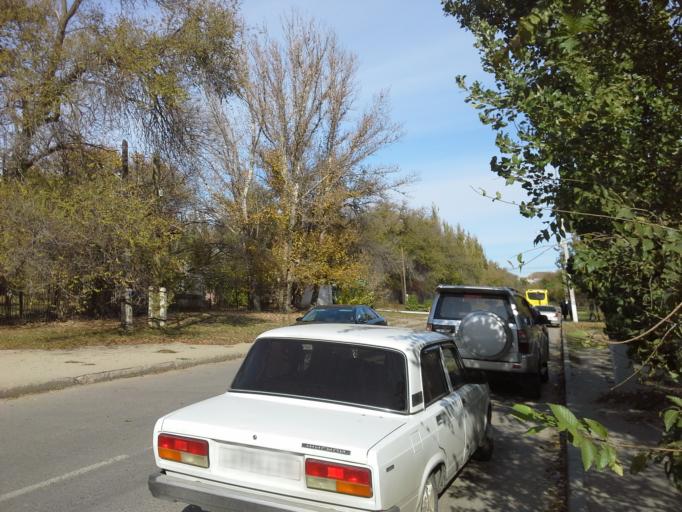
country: RU
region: Volgograd
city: Vodstroy
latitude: 48.8400
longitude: 44.6379
